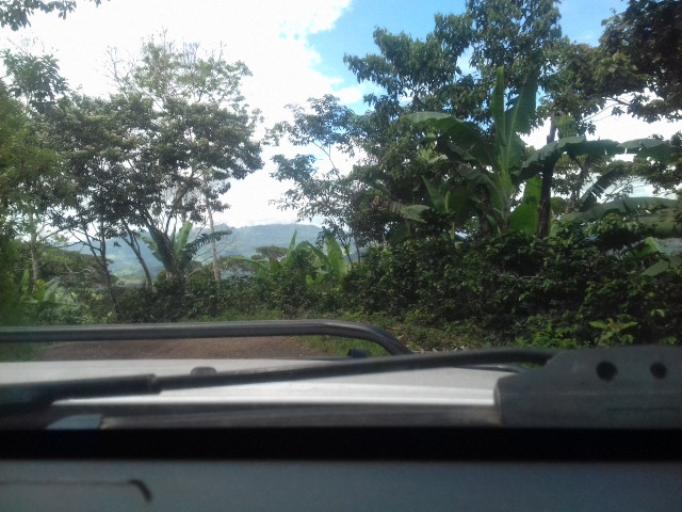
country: NI
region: Atlantico Norte (RAAN)
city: Waslala
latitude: 13.2113
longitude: -85.5761
